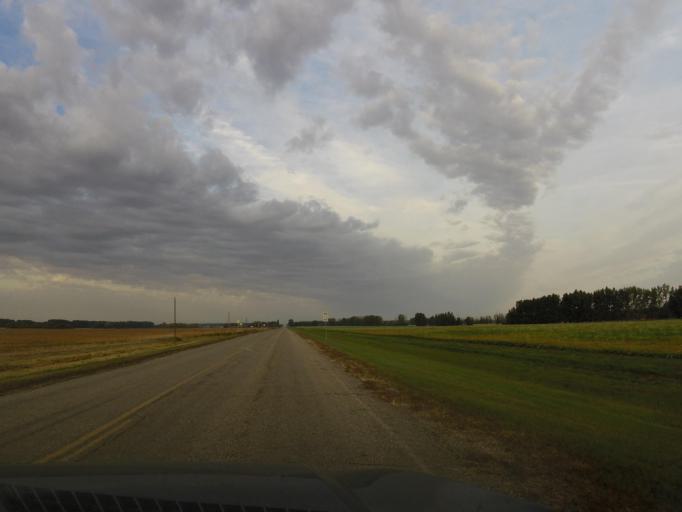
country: US
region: North Dakota
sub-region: Pembina County
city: Cavalier
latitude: 48.6882
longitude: -97.6236
